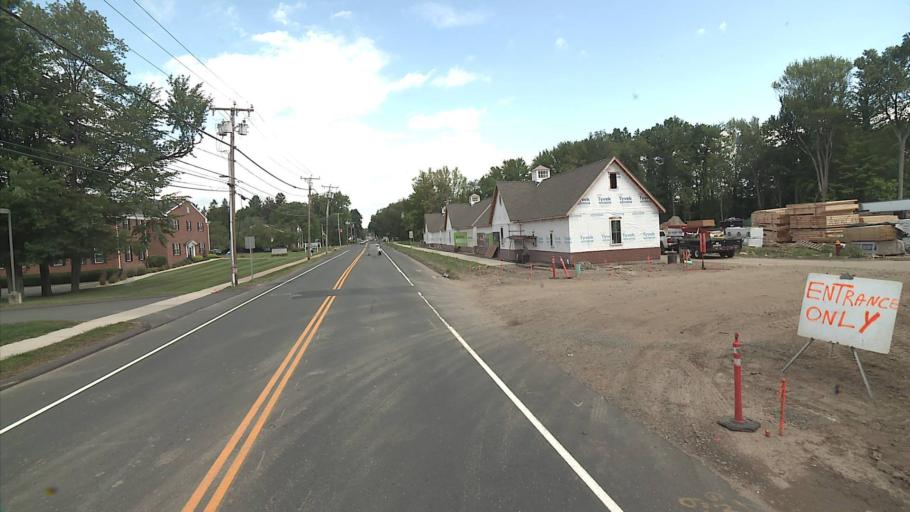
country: US
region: Connecticut
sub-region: Hartford County
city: Blue Hills
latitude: 41.8276
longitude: -72.7374
